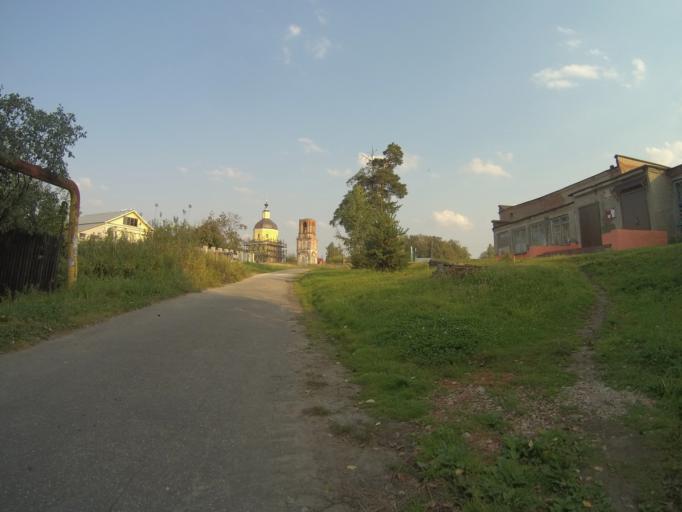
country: RU
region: Vladimir
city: Orgtrud
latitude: 56.2073
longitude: 40.5815
